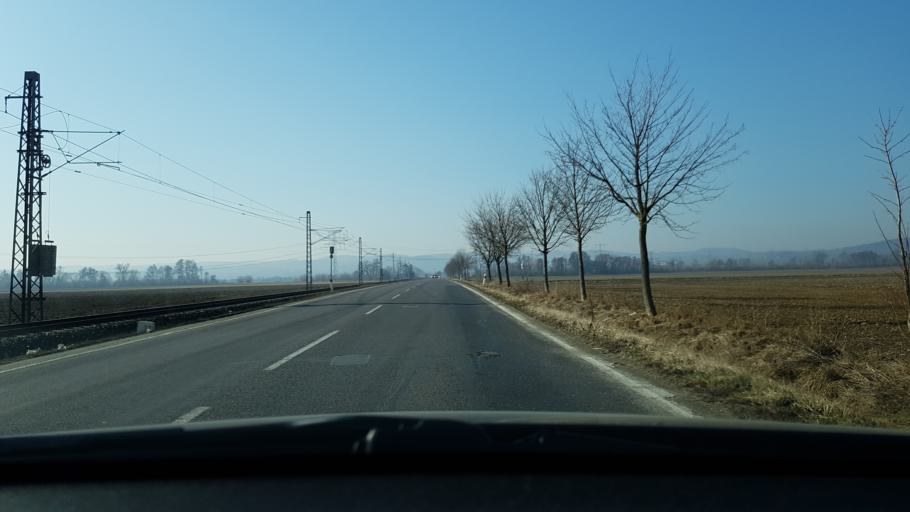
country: CZ
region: Olomoucky
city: Postrelmov
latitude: 49.9013
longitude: 16.9098
